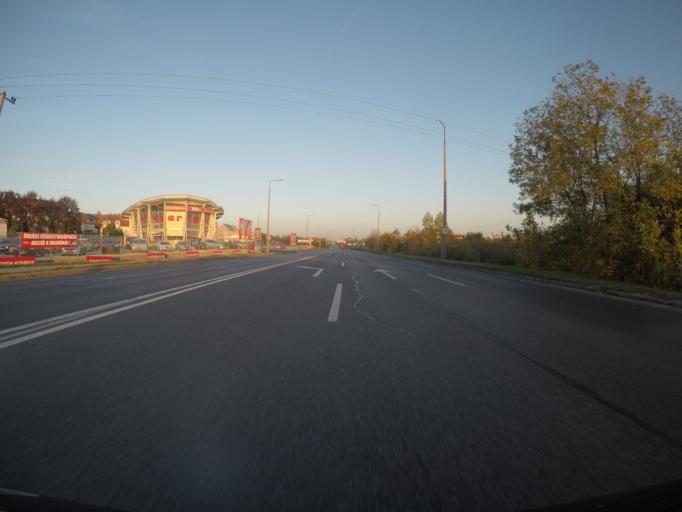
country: HU
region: Baranya
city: Pellerd
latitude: 46.0652
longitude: 18.1643
